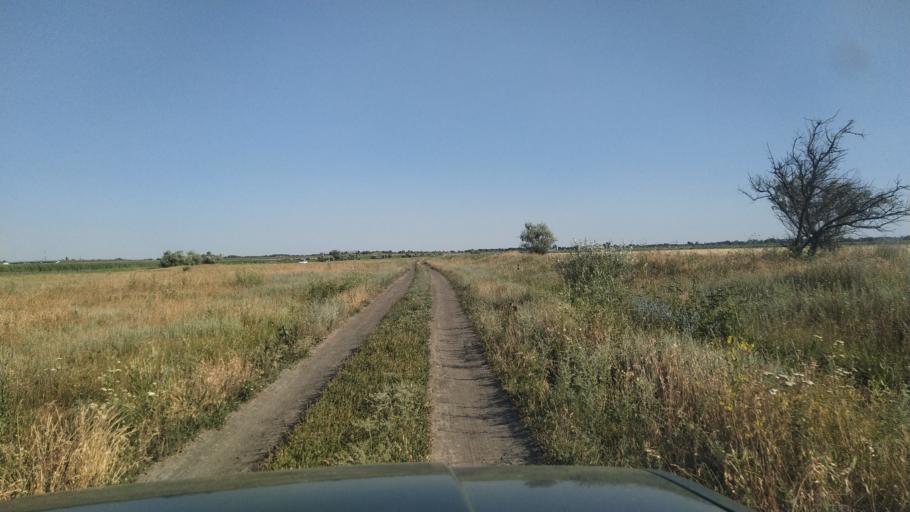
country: RU
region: Rostov
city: Kuleshovka
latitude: 47.1284
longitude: 39.6449
